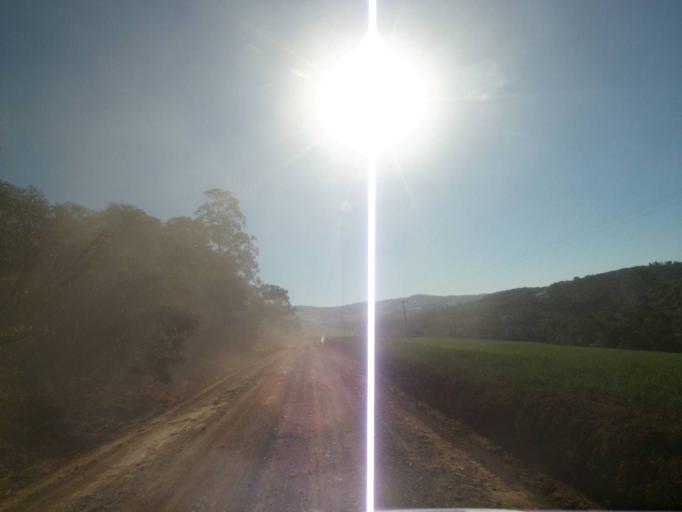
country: BR
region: Parana
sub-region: Tibagi
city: Tibagi
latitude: -24.5316
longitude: -50.4866
